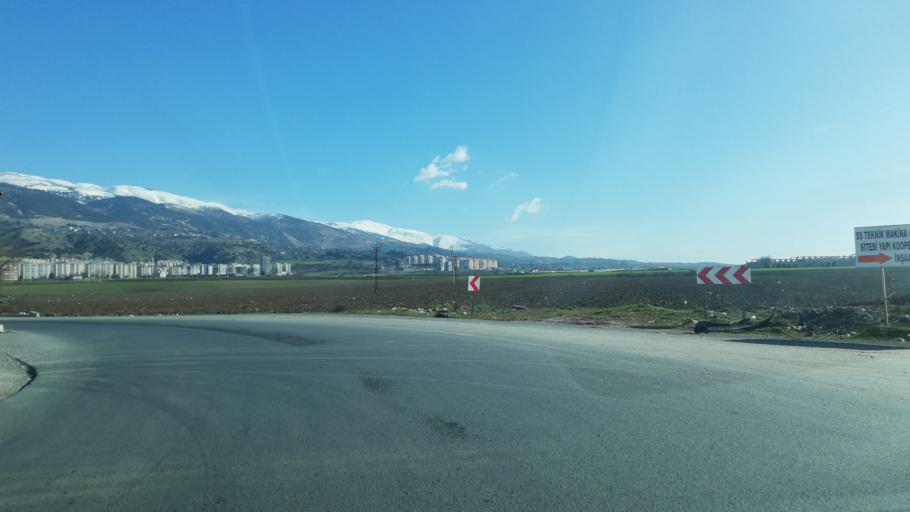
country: TR
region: Kahramanmaras
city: Kahramanmaras
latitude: 37.5715
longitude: 36.9744
